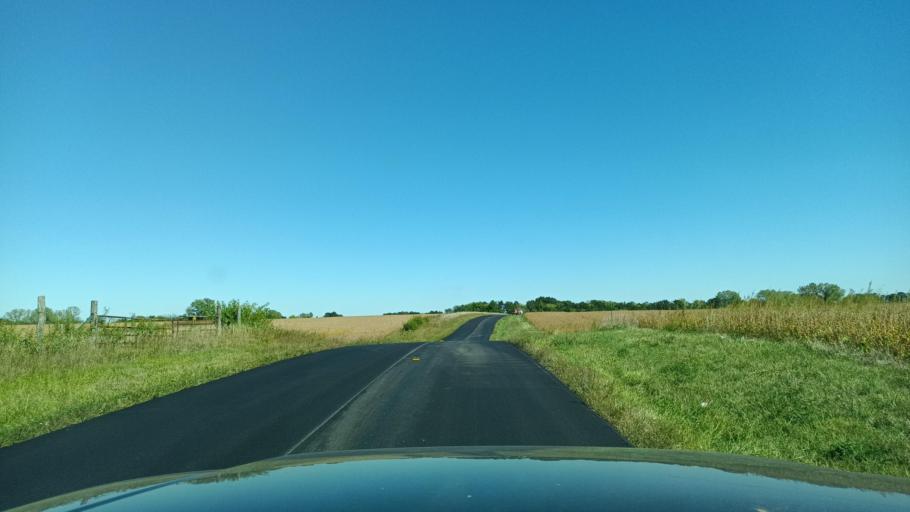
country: US
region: Missouri
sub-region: Macon County
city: La Plata
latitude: 39.9272
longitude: -92.5441
